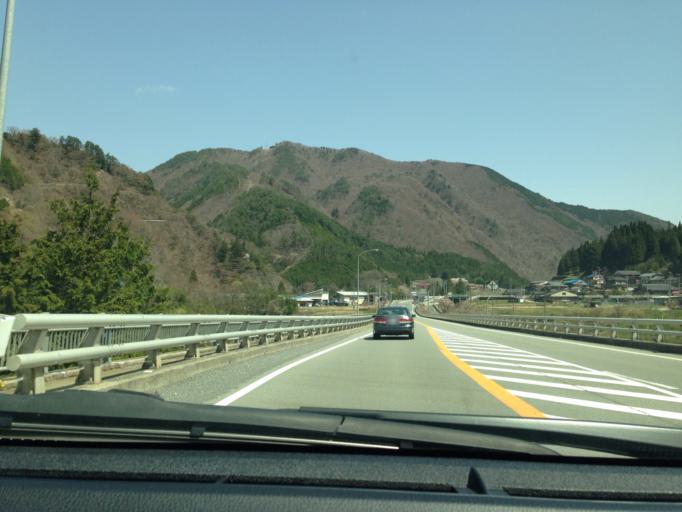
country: JP
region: Gifu
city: Takayama
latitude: 35.9669
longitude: 137.2598
